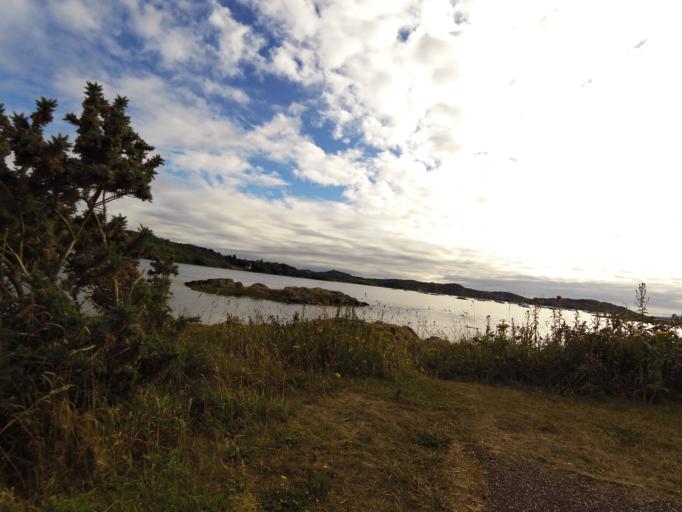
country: GB
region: Scotland
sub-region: Argyll and Bute
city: Isle Of Mull
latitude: 56.9095
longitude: -5.8468
